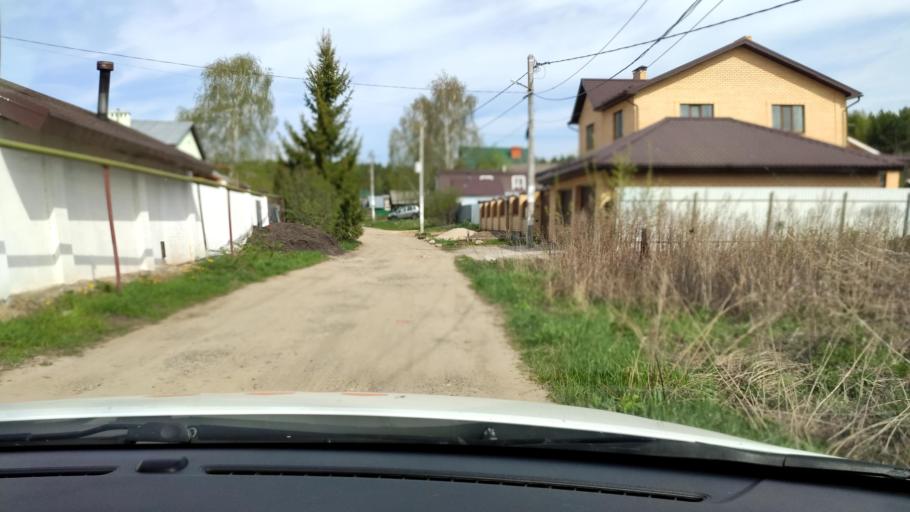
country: RU
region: Tatarstan
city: Osinovo
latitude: 55.8073
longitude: 48.8857
